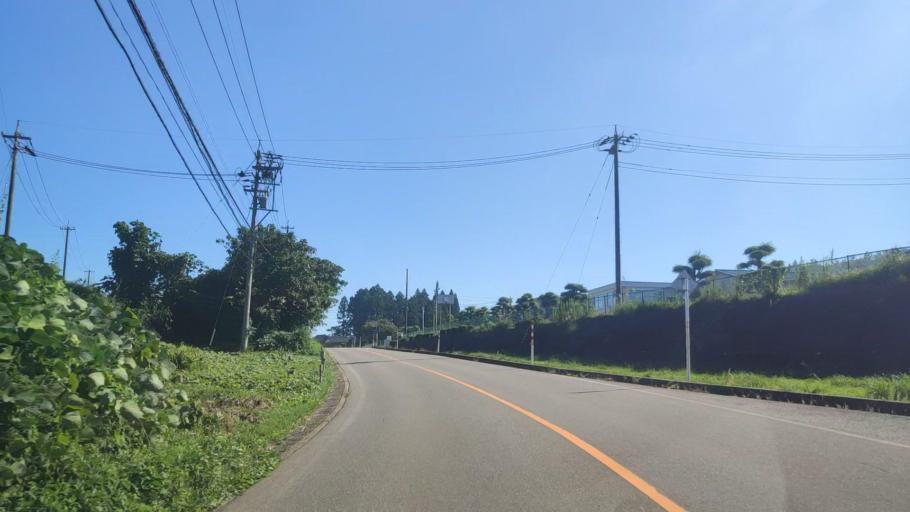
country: JP
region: Ishikawa
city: Nanao
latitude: 37.3450
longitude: 137.2278
